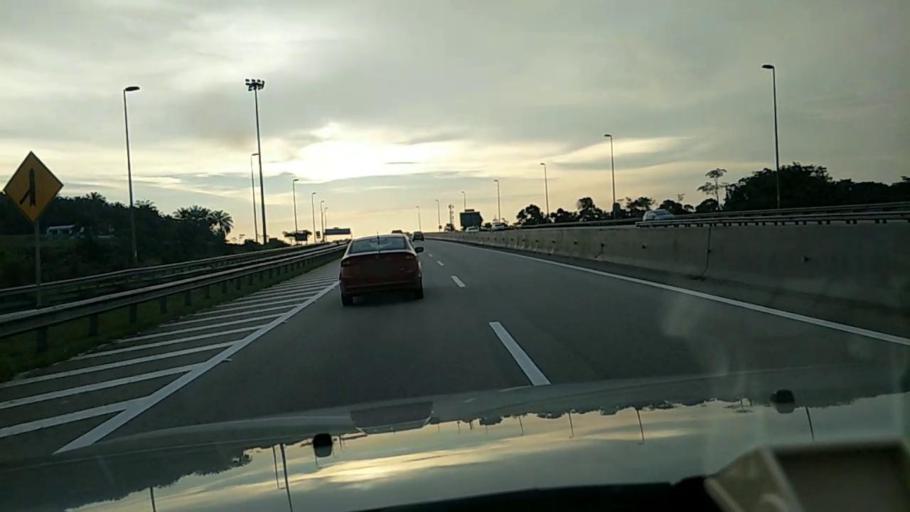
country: MY
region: Selangor
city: Kuang
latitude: 3.2706
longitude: 101.5430
